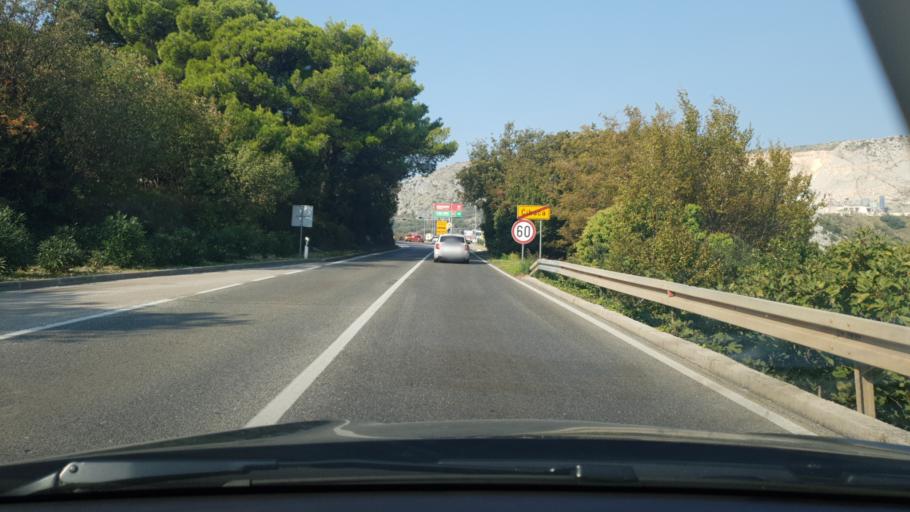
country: HR
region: Dubrovacko-Neretvanska
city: Cibaca
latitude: 42.6283
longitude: 18.1639
